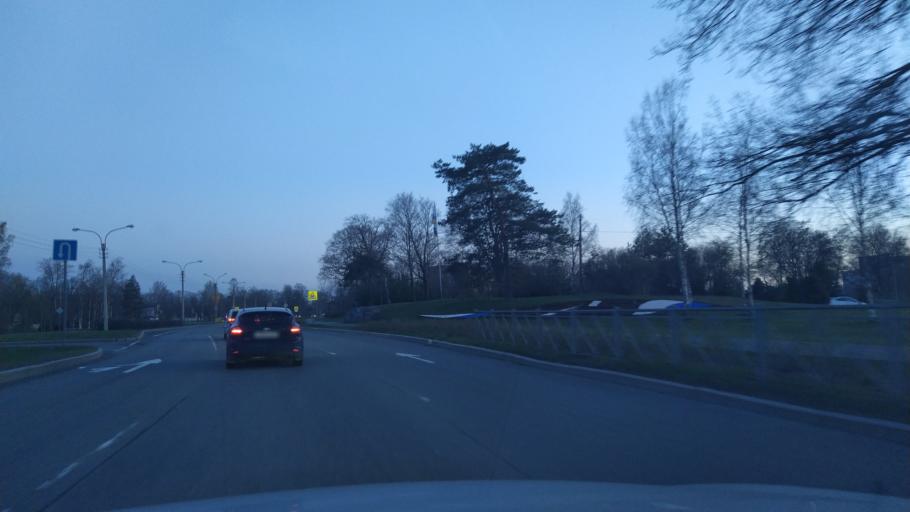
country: RU
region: St.-Petersburg
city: Sestroretsk
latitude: 60.0932
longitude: 29.9761
